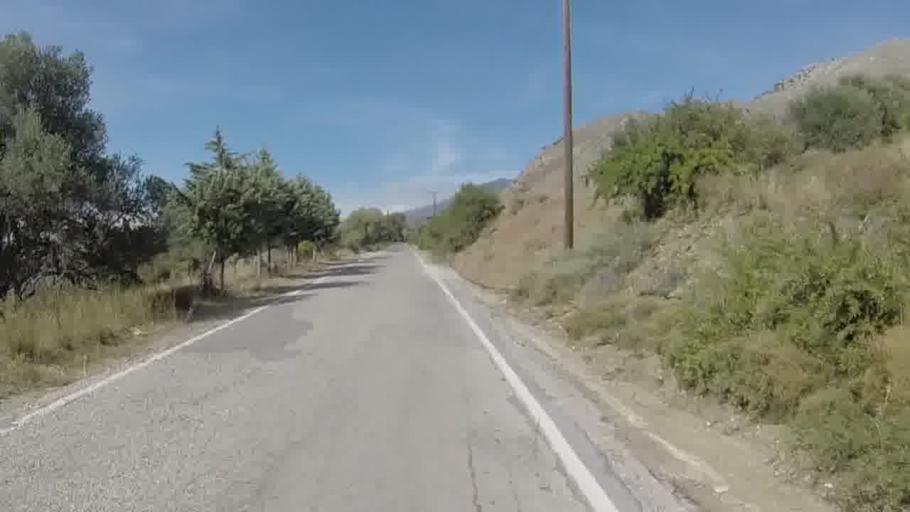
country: GR
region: Crete
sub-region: Nomos Rethymnis
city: Agia Galini
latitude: 35.1502
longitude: 24.7361
